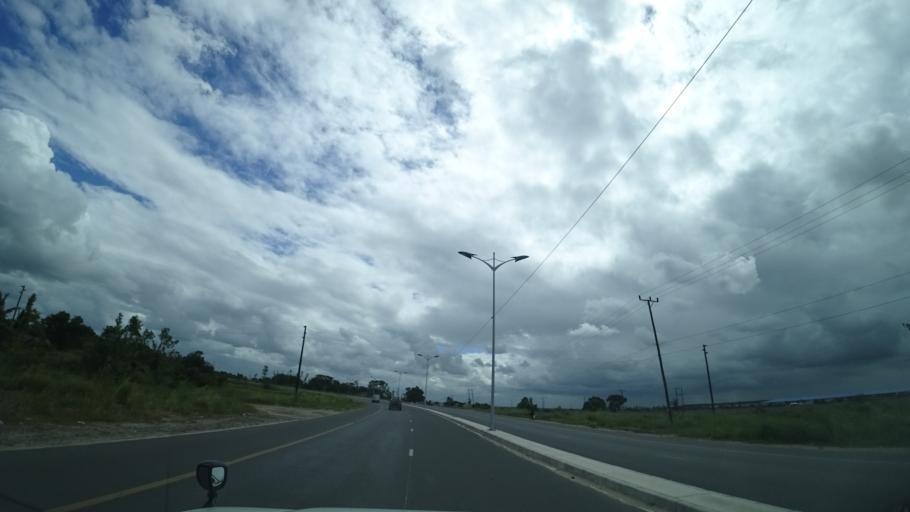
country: MZ
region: Sofala
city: Dondo
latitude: -19.5820
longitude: 34.7344
